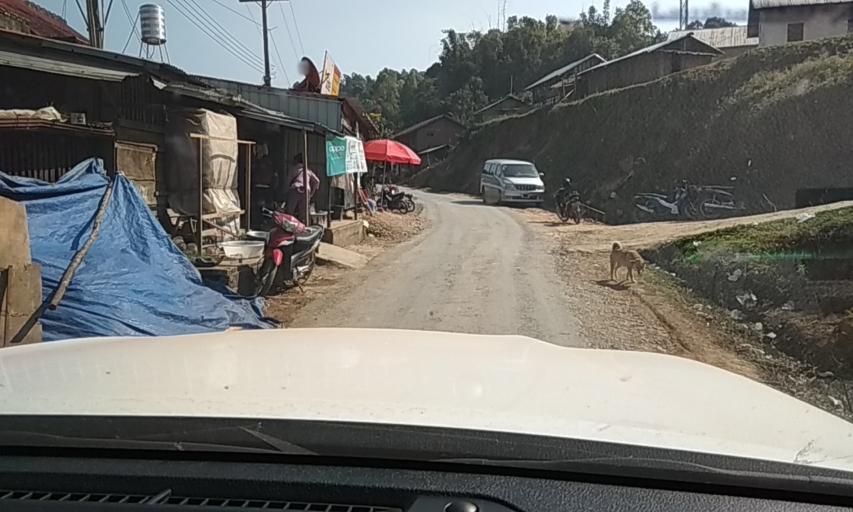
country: LA
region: Phongsali
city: Phongsali
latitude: 21.6636
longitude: 102.0893
